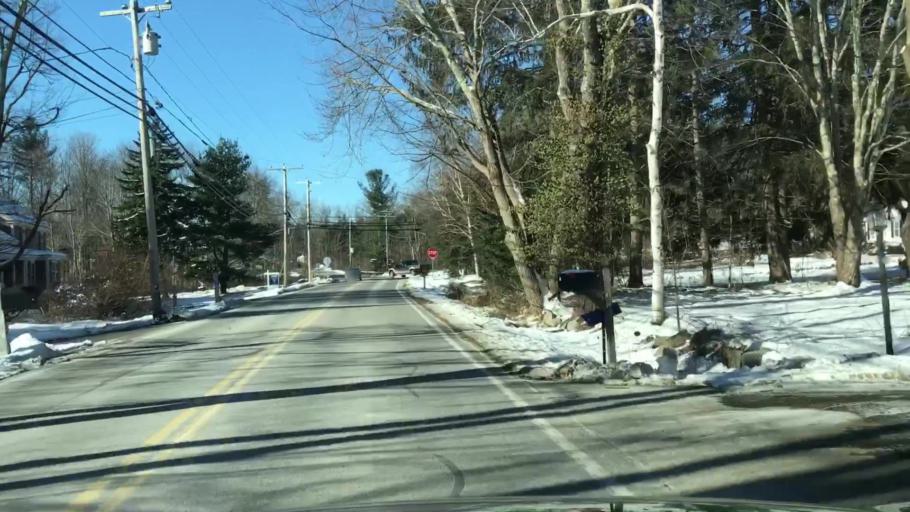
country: US
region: New Hampshire
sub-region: Hillsborough County
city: Bedford
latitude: 42.9431
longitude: -71.5267
